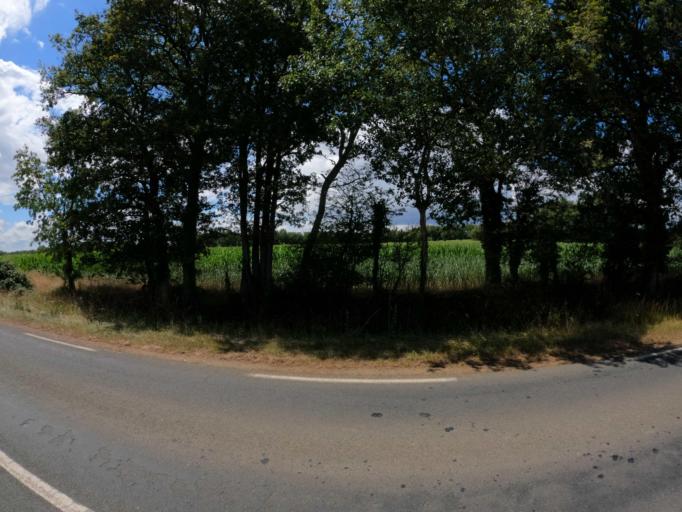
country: FR
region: Pays de la Loire
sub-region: Departement de la Sarthe
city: Brulon
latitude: 47.9334
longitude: -0.2595
